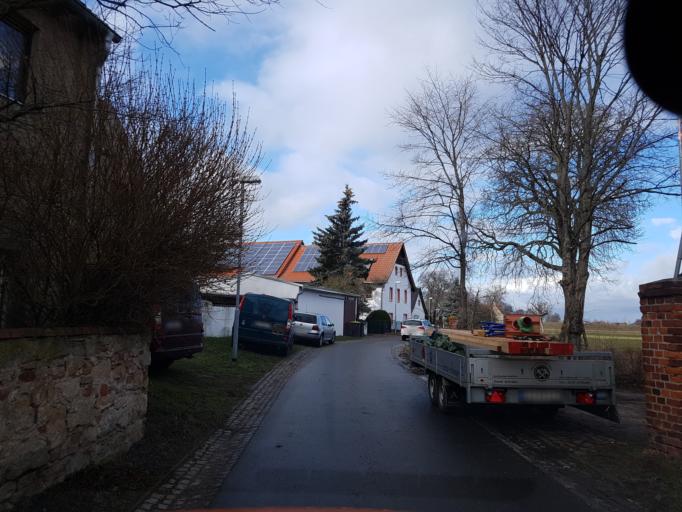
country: DE
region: Brandenburg
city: Muhlberg
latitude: 51.4814
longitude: 13.1932
